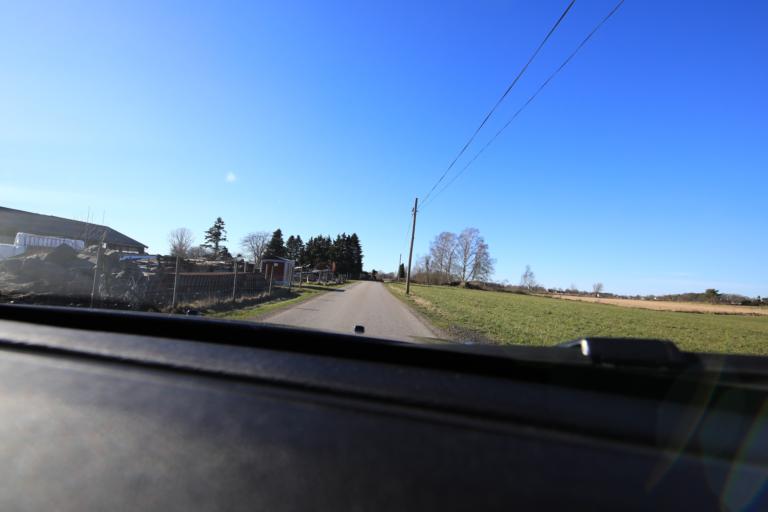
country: SE
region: Halland
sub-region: Varbergs Kommun
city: Tvaaker
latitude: 57.0653
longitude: 12.3893
